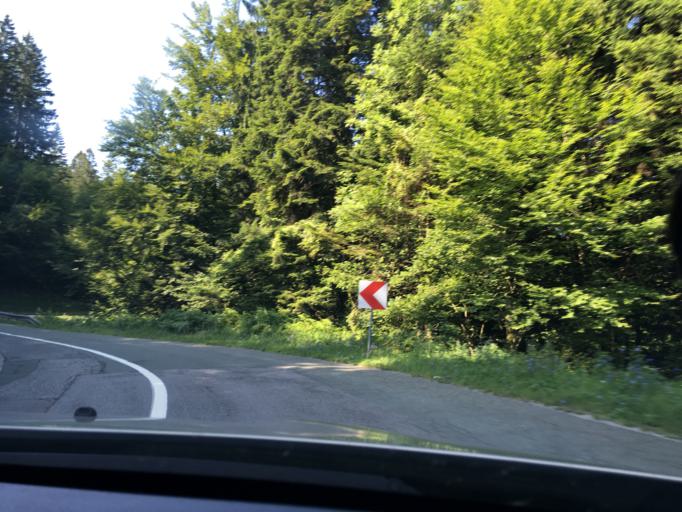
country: HR
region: Primorsko-Goranska
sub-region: Grad Delnice
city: Delnice
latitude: 45.4103
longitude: 14.8163
